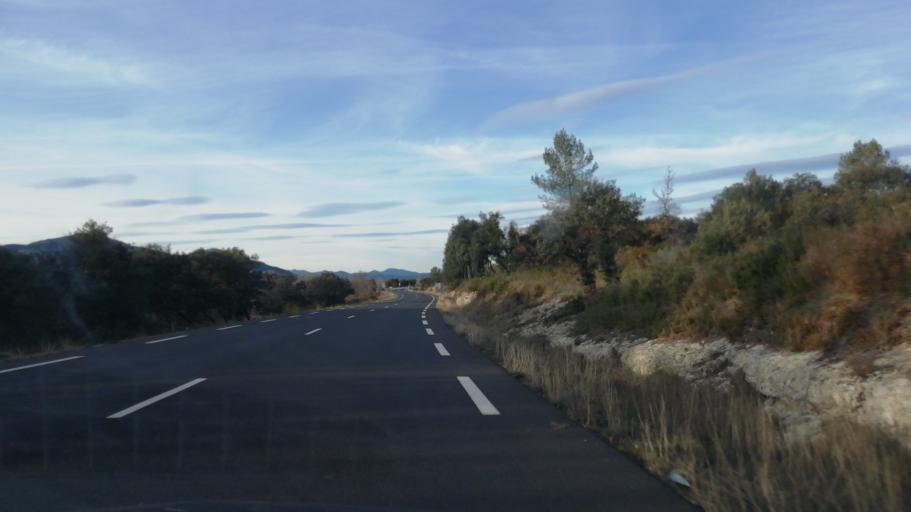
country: FR
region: Languedoc-Roussillon
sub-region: Departement du Gard
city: Quissac
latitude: 43.8884
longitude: 4.0147
